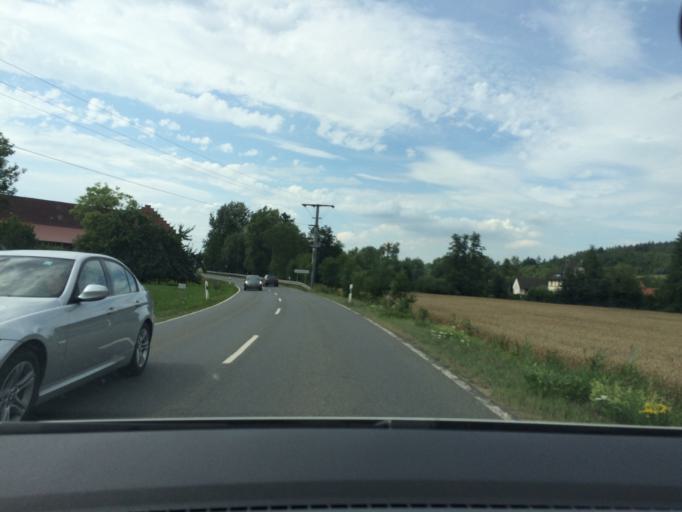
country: DE
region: Bavaria
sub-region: Regierungsbezirk Unterfranken
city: Sailauf
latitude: 49.9894
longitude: 9.2524
